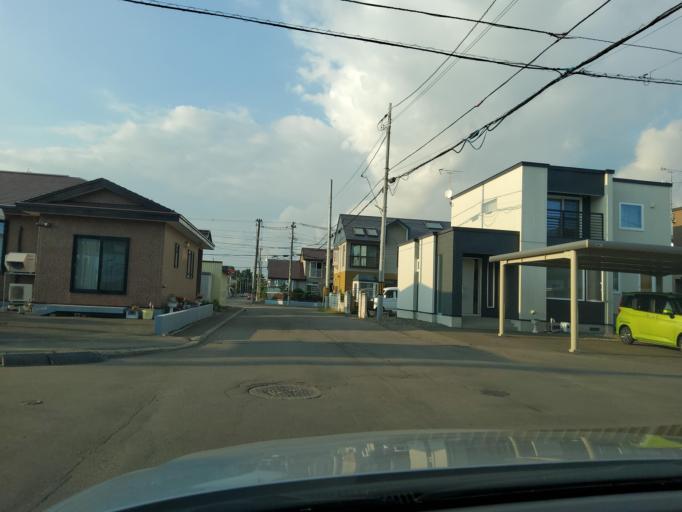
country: JP
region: Hokkaido
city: Obihiro
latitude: 42.9206
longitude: 143.1555
